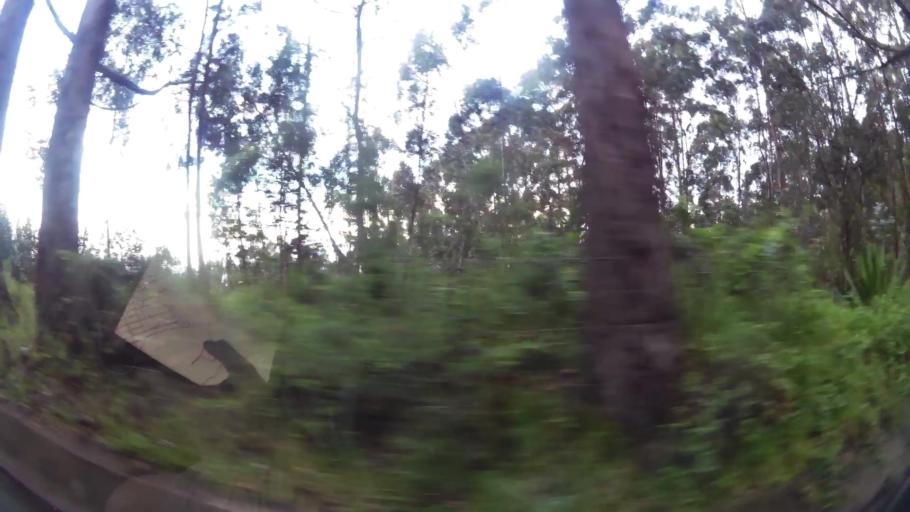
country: EC
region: Pichincha
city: Quito
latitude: -0.1085
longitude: -78.5221
